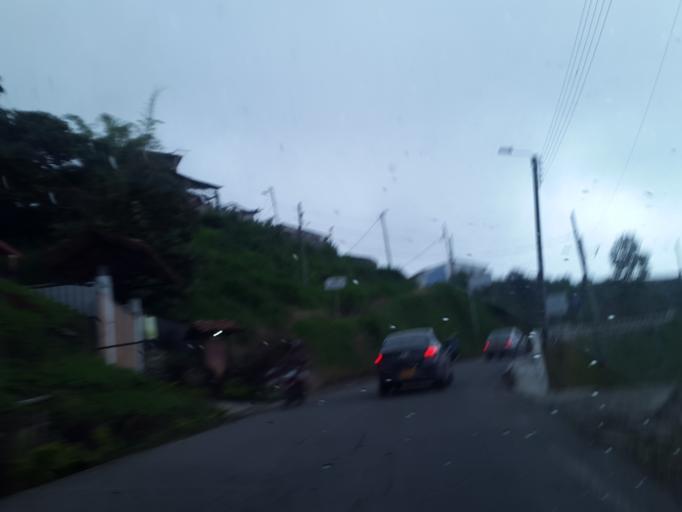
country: CO
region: Quindio
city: Salento
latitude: 4.6416
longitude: -75.5719
